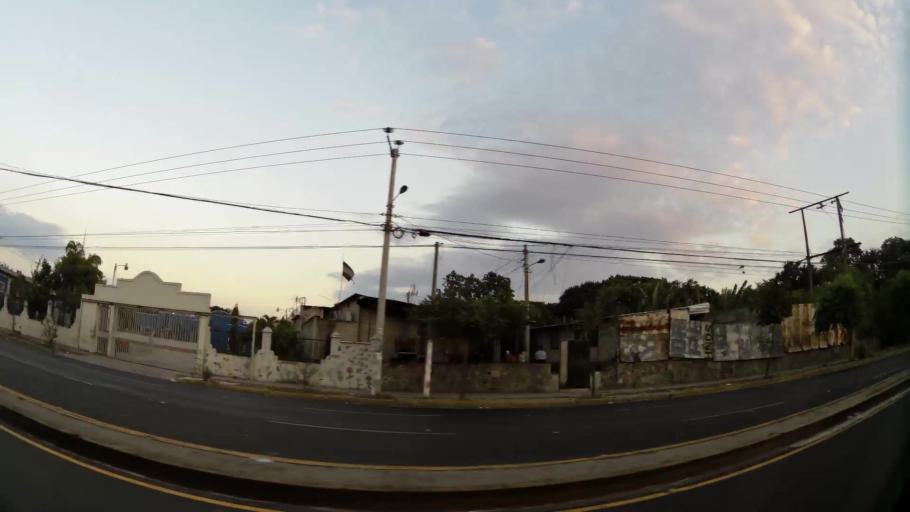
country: SV
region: San Salvador
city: Delgado
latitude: 13.7087
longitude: -89.1773
